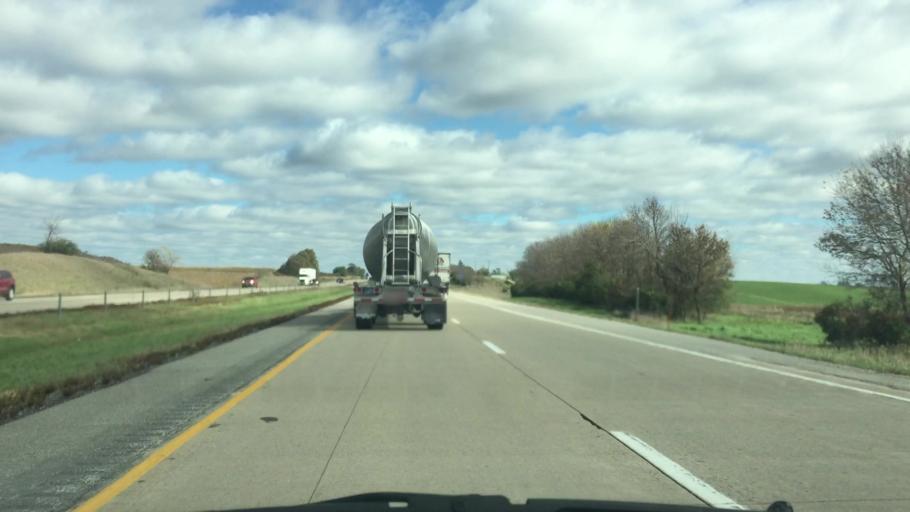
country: US
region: Iowa
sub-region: Poweshiek County
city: Brooklyn
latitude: 41.6960
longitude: -92.4382
